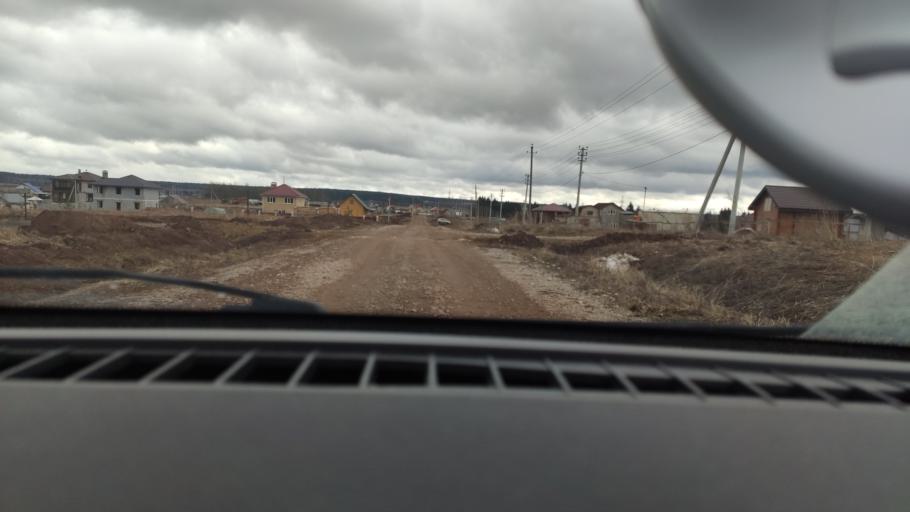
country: RU
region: Perm
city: Ferma
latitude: 57.9491
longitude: 56.3387
